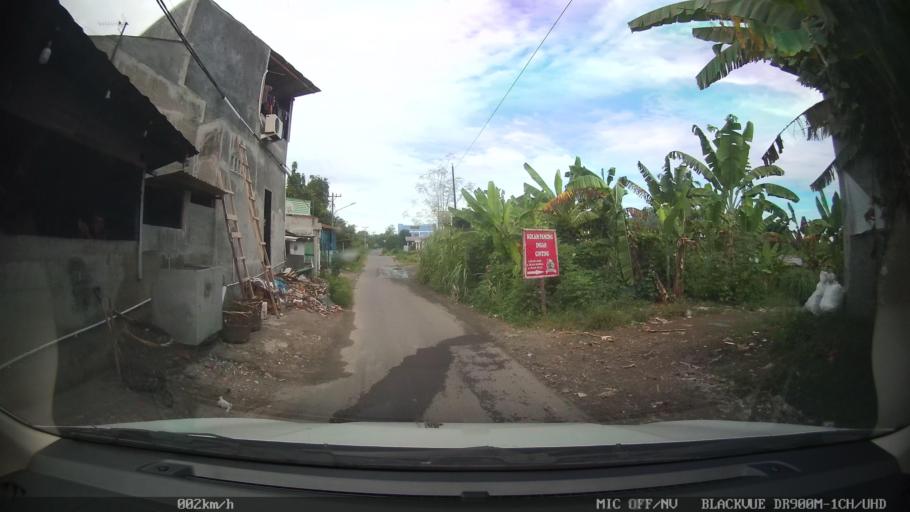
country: ID
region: North Sumatra
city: Sunggal
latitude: 3.5729
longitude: 98.5846
